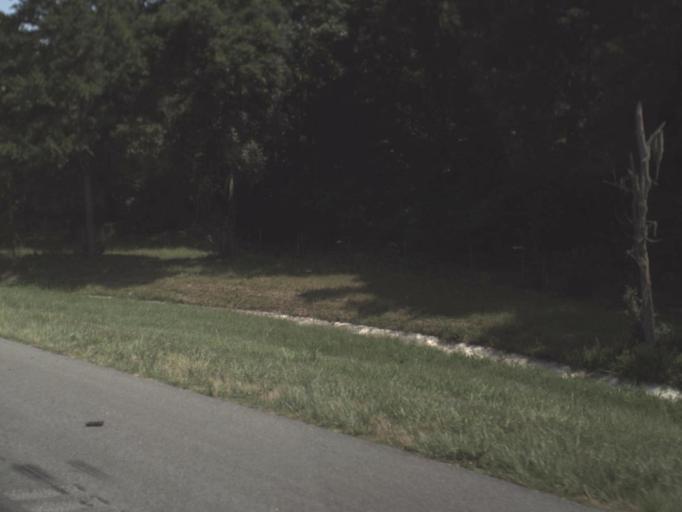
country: US
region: Florida
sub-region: Hamilton County
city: Jasper
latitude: 30.5475
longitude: -83.0773
